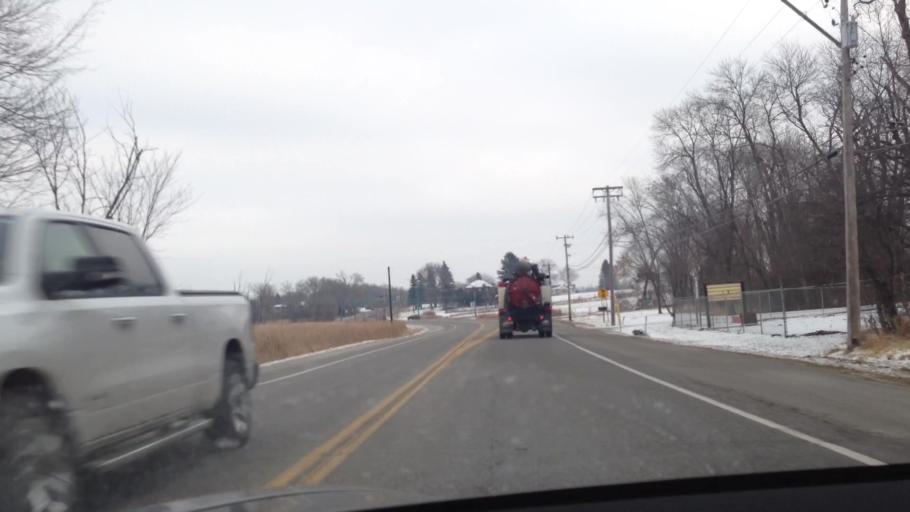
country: US
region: Minnesota
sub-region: Washington County
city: Forest Lake
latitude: 45.2528
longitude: -93.0025
